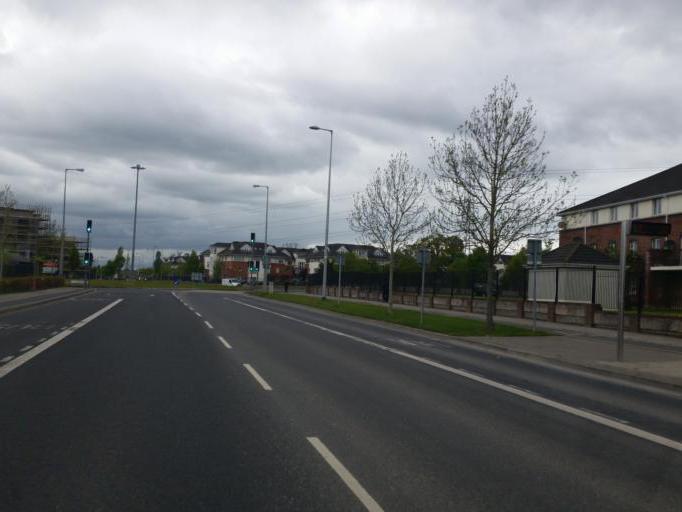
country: IE
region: Leinster
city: Hartstown
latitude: 53.3907
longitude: -6.4297
